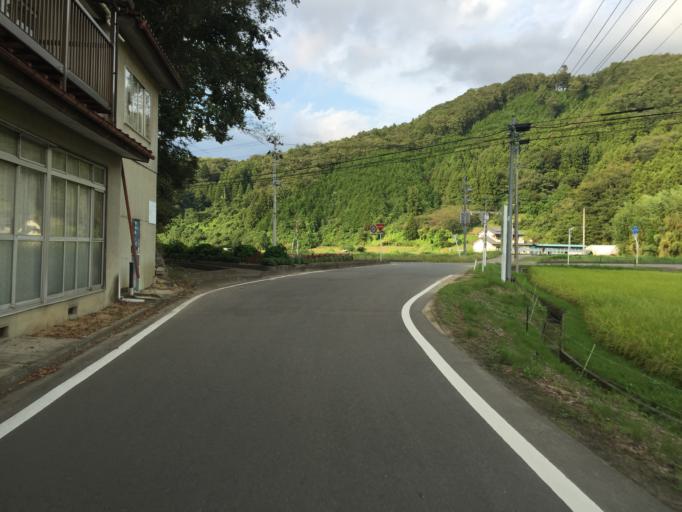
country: JP
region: Fukushima
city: Hobaramachi
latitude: 37.7199
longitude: 140.6055
